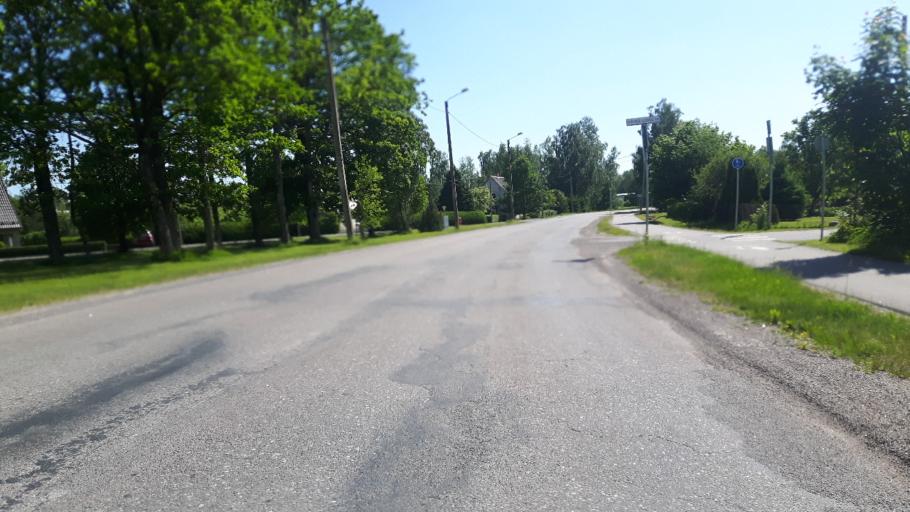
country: EE
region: Paernumaa
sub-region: Sindi linn
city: Sindi
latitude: 58.4003
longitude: 24.6460
